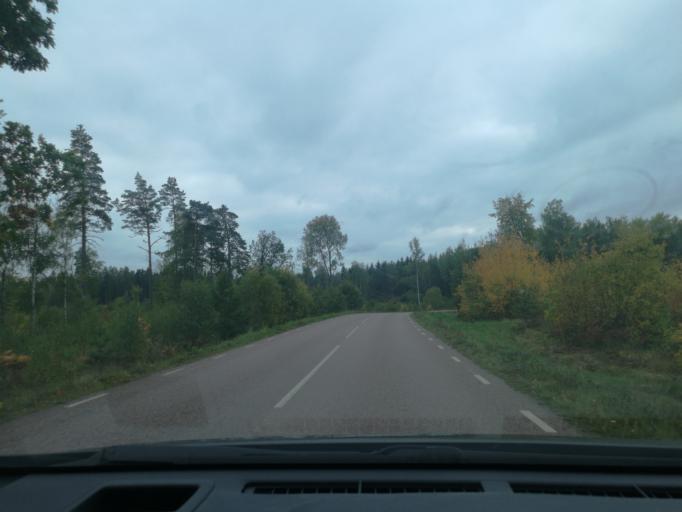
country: SE
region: Vaestmanland
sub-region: Vasteras
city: Tillberga
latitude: 59.7227
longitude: 16.6684
